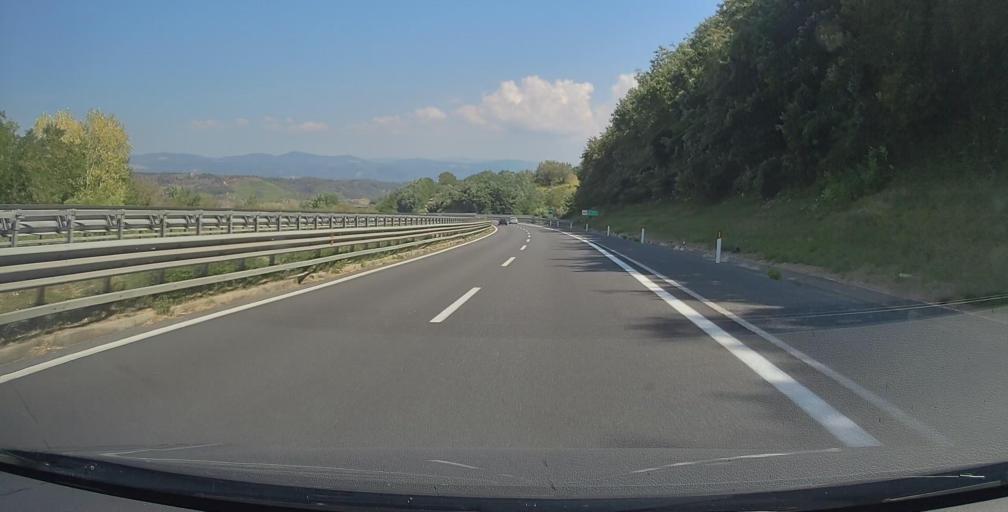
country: IT
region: Calabria
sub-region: Provincia di Vibo-Valentia
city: Sant'Onofrio
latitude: 38.6851
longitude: 16.1627
